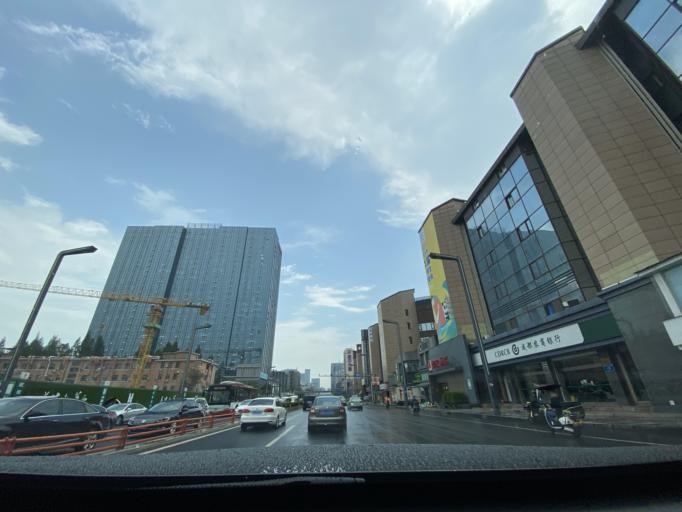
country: CN
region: Sichuan
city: Chengdu
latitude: 30.6342
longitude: 104.0737
